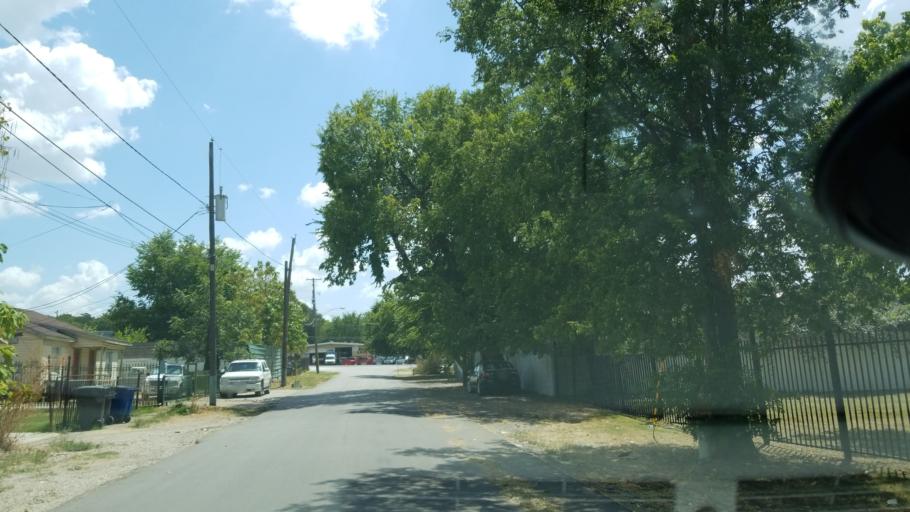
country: US
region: Texas
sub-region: Dallas County
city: Cockrell Hill
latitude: 32.7452
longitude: -96.9062
